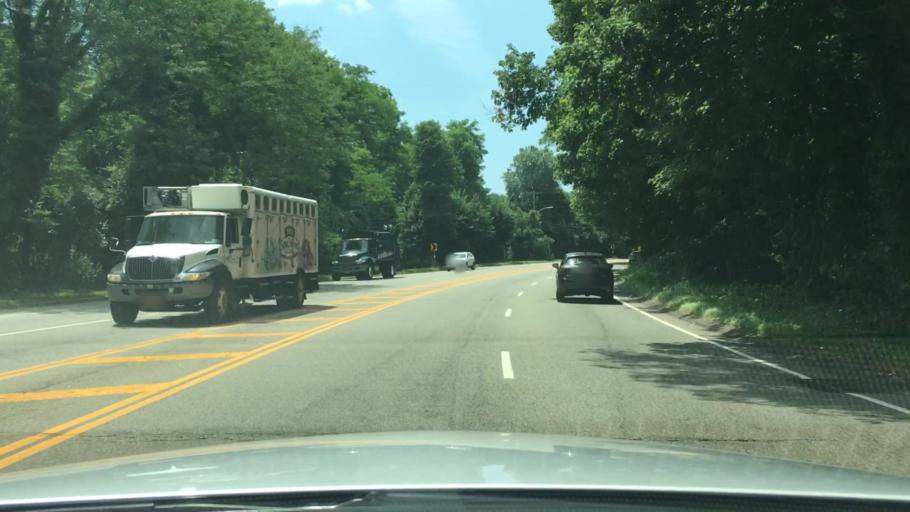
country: US
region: New York
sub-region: Suffolk County
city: West Hills
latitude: 40.8211
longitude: -73.4459
